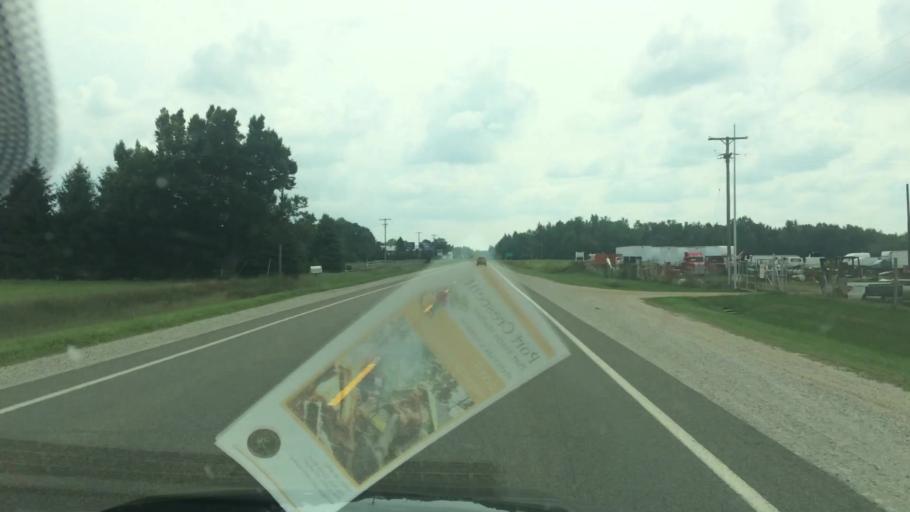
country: US
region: Michigan
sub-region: Tuscola County
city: Cass City
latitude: 43.6654
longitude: -83.0983
